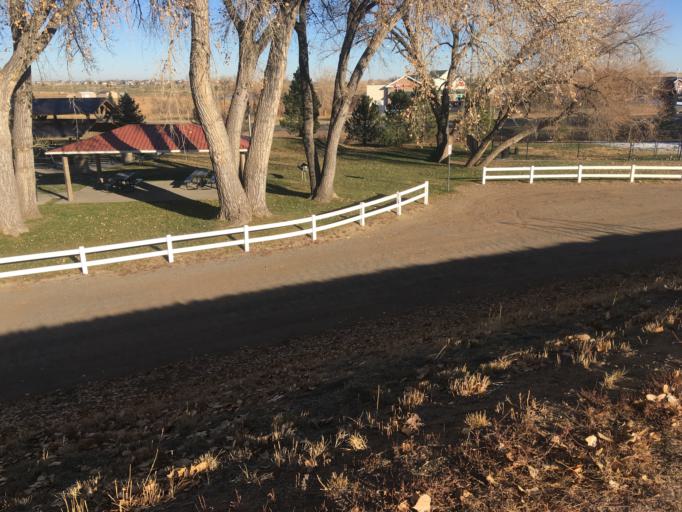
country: US
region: Colorado
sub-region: Weld County
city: Firestone
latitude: 40.1221
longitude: -104.9431
